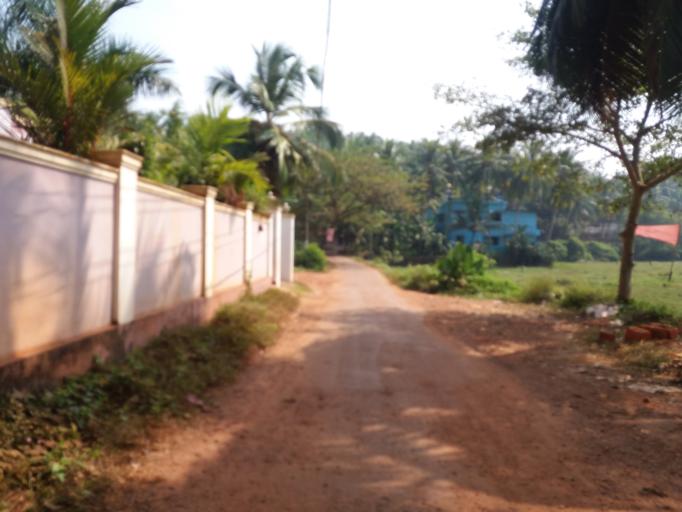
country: IN
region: Kerala
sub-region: Kozhikode
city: Kunnamangalam
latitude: 11.3005
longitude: 75.8210
